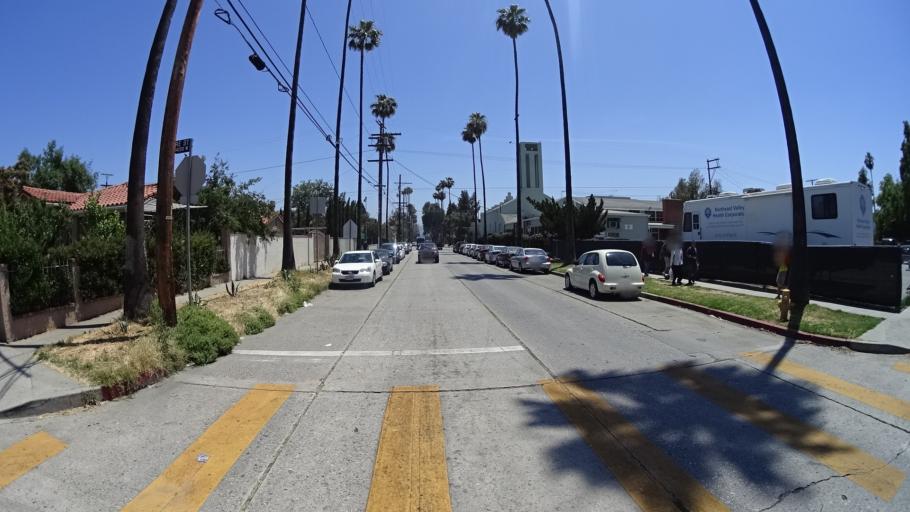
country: US
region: California
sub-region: Los Angeles County
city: Van Nuys
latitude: 34.1876
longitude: -118.4443
